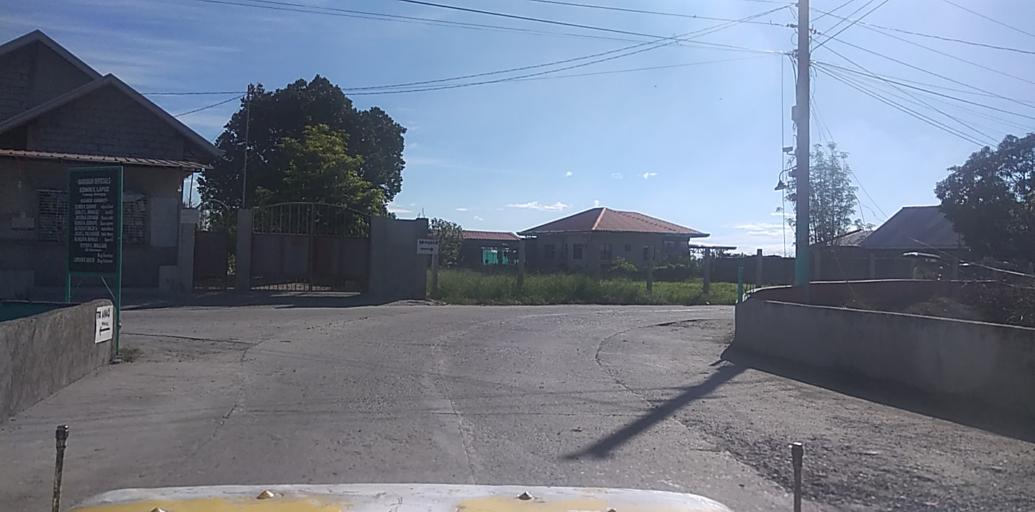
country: PH
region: Central Luzon
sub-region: Province of Pampanga
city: San Patricio
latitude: 15.1124
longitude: 120.7113
